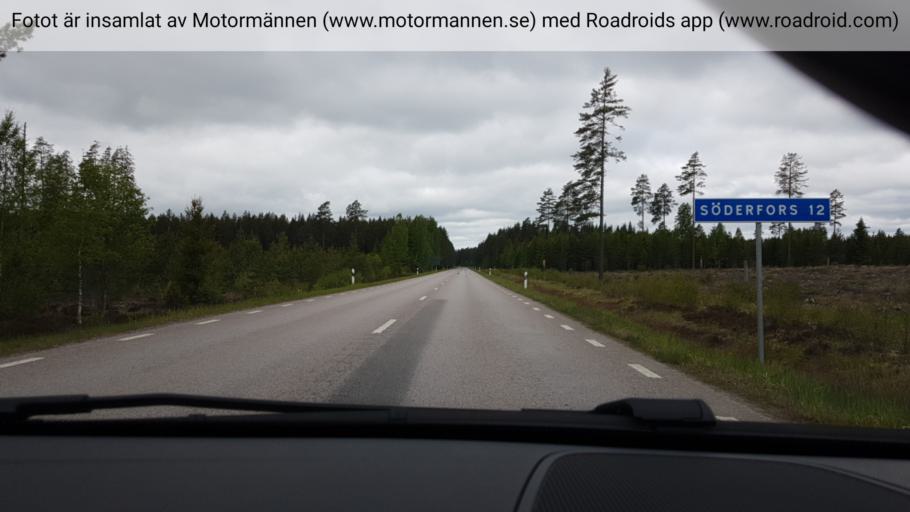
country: SE
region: Uppsala
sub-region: Tierps Kommun
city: Tierp
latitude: 60.3566
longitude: 17.4478
